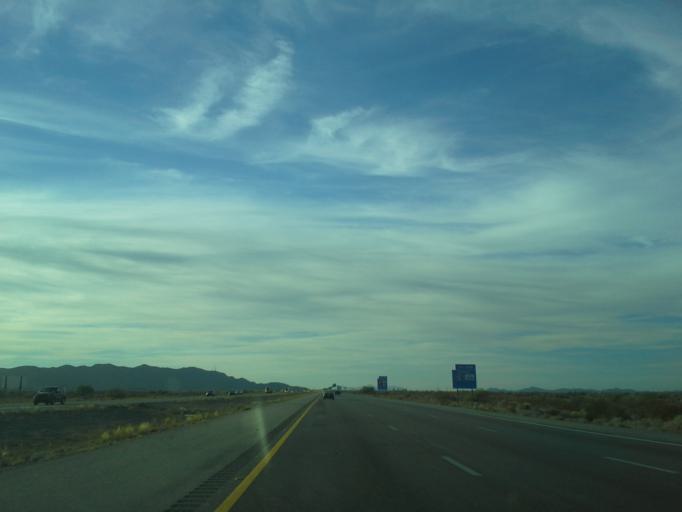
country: US
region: Arizona
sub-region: Pinal County
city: Arizona City
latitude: 32.7908
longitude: -111.6410
